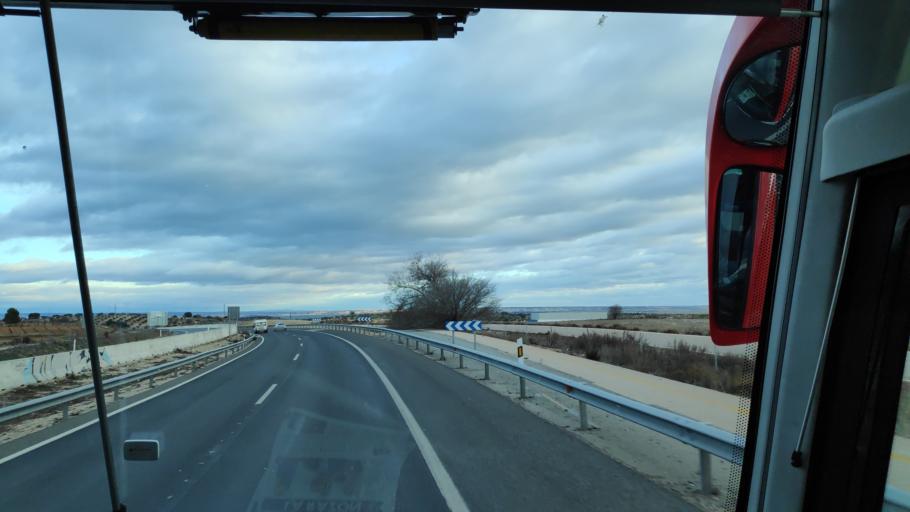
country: ES
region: Madrid
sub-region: Provincia de Madrid
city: Villarejo de Salvanes
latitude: 40.1575
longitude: -3.2594
